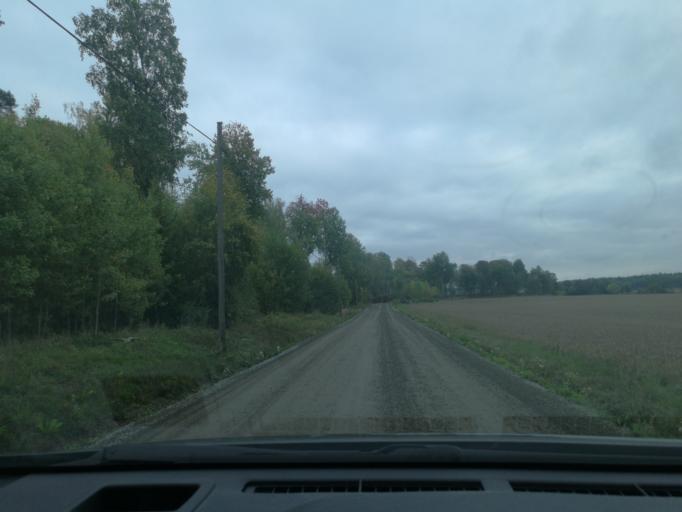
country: SE
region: Vaestmanland
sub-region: Vasteras
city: Tillberga
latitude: 59.7407
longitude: 16.6974
